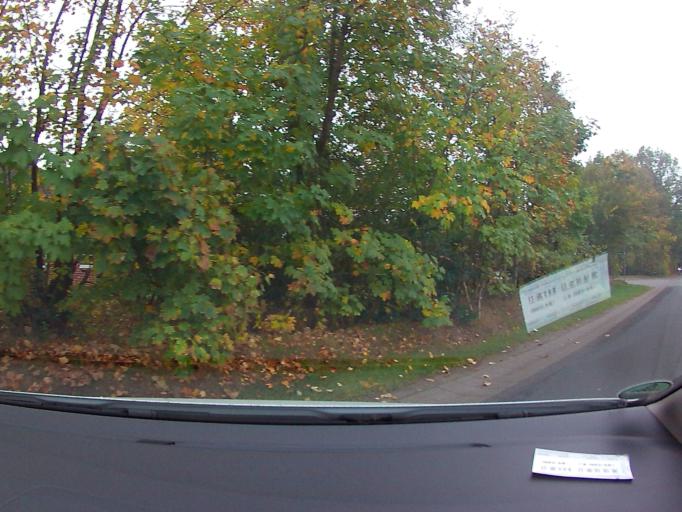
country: DE
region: Schleswig-Holstein
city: Breklum
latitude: 54.6156
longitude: 8.9890
